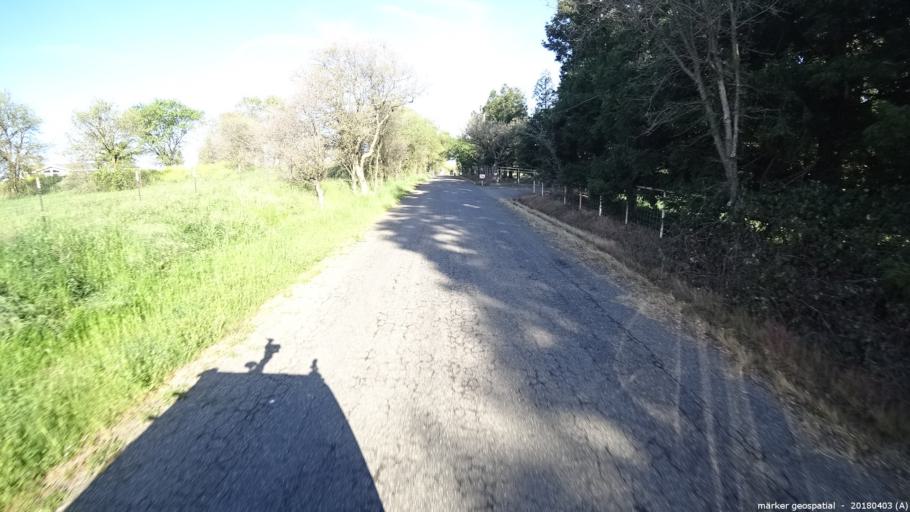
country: US
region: California
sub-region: Sacramento County
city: Wilton
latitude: 38.4396
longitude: -121.2087
